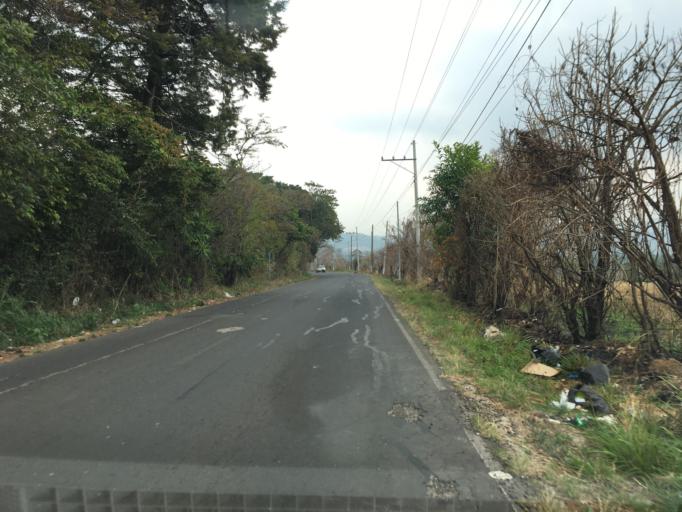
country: GT
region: Guatemala
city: Fraijanes
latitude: 14.3818
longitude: -90.4890
